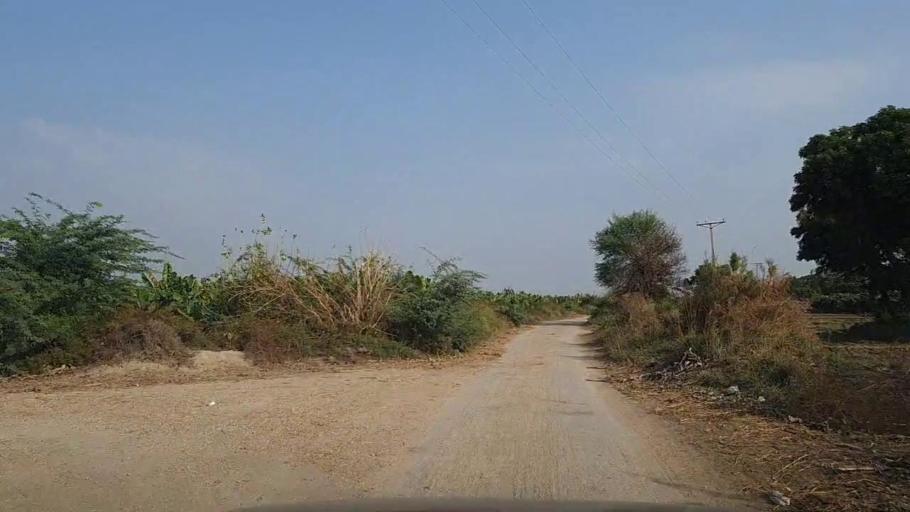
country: PK
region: Sindh
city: Thatta
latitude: 24.6458
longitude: 67.9371
